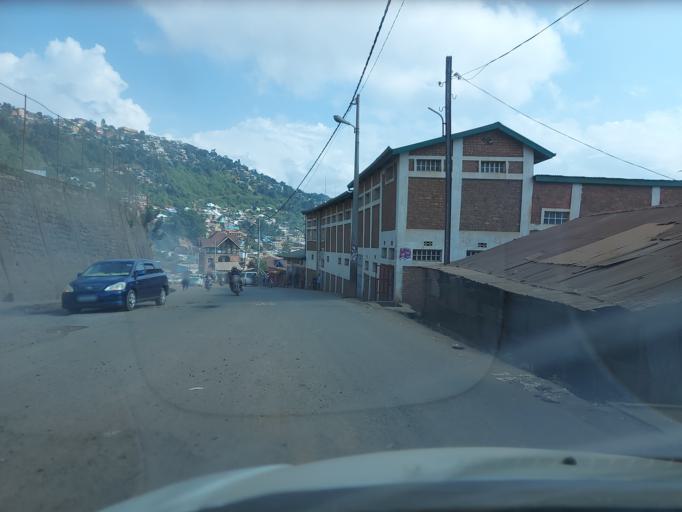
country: CD
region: South Kivu
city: Bukavu
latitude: -2.5160
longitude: 28.8502
